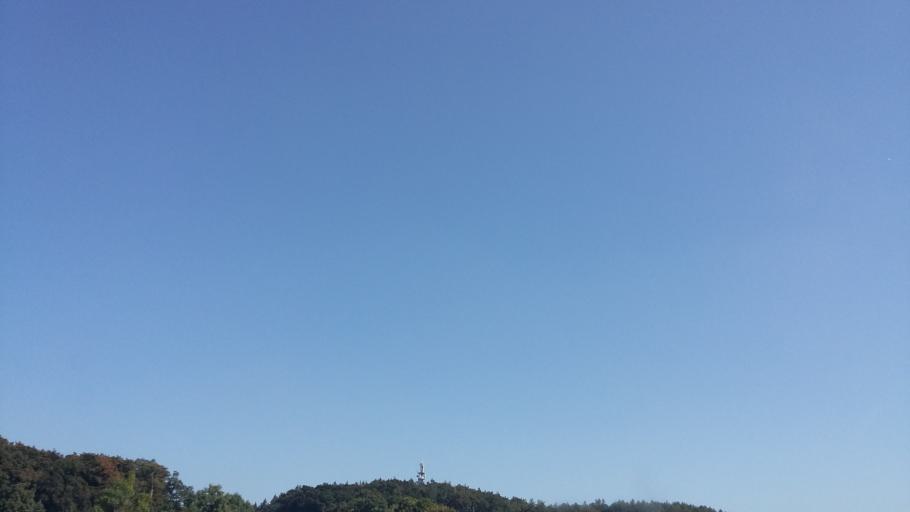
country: DE
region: Bavaria
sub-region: Upper Bavaria
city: Inning am Ammersee
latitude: 48.0834
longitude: 11.1635
